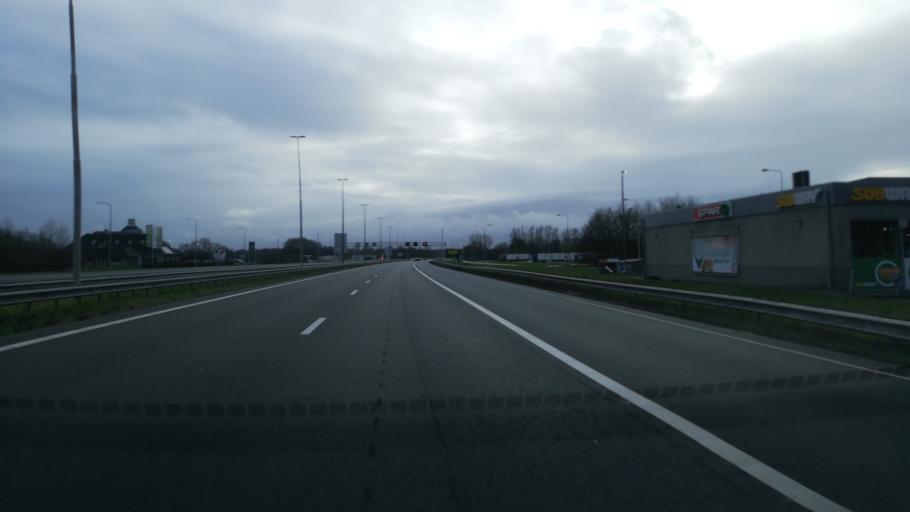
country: NL
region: Gelderland
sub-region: Gemeente Apeldoorn
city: Loenen
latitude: 52.1712
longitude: 6.0271
